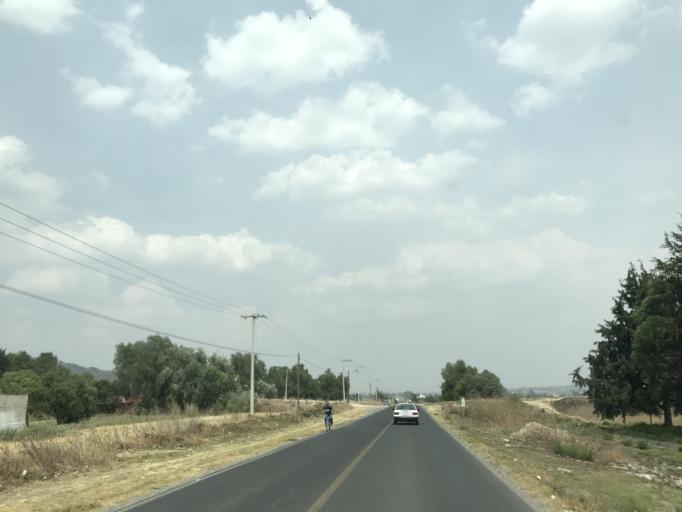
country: MX
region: Tlaxcala
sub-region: Panotla
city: Fraccionamiento la Virgen
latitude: 19.3212
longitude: -98.2967
